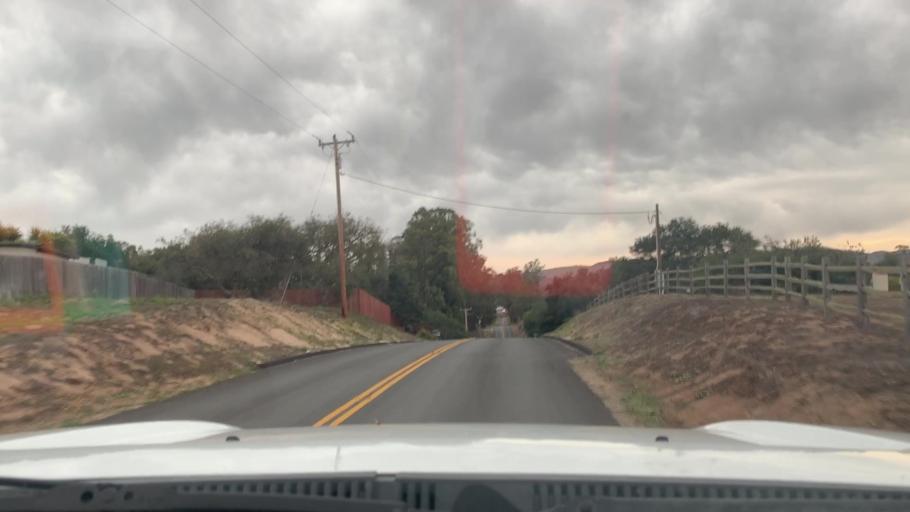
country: US
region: California
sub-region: San Luis Obispo County
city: Callender
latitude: 35.0658
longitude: -120.5559
